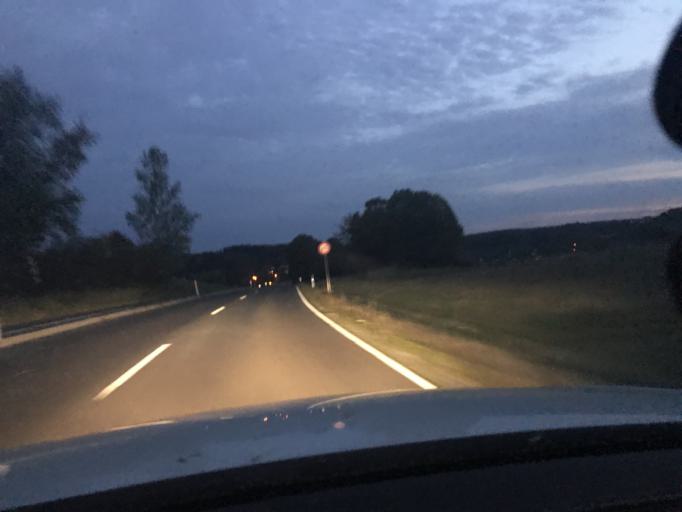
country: DE
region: Bavaria
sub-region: Upper Franconia
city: Pegnitz
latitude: 49.7515
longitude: 11.5606
